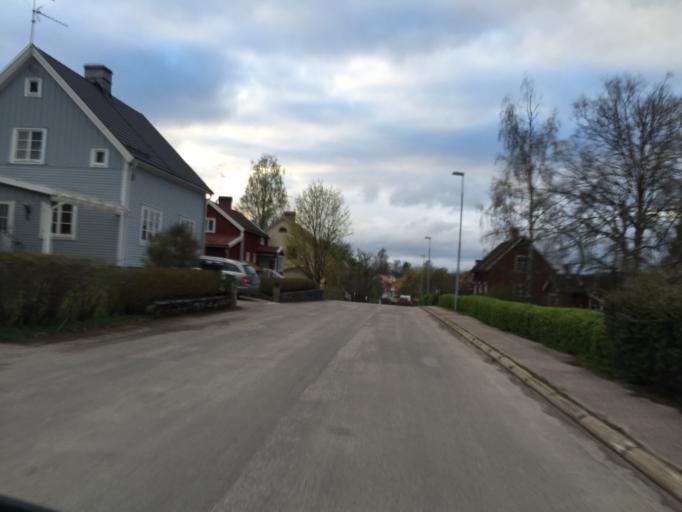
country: SE
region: Dalarna
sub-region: Ludvika Kommun
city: Ludvika
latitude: 60.1405
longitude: 15.1978
